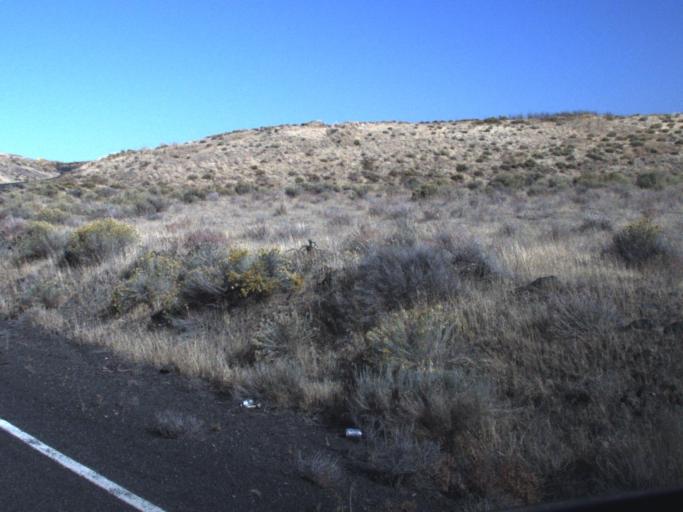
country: US
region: Washington
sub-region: Franklin County
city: Connell
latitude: 46.5686
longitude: -118.5397
